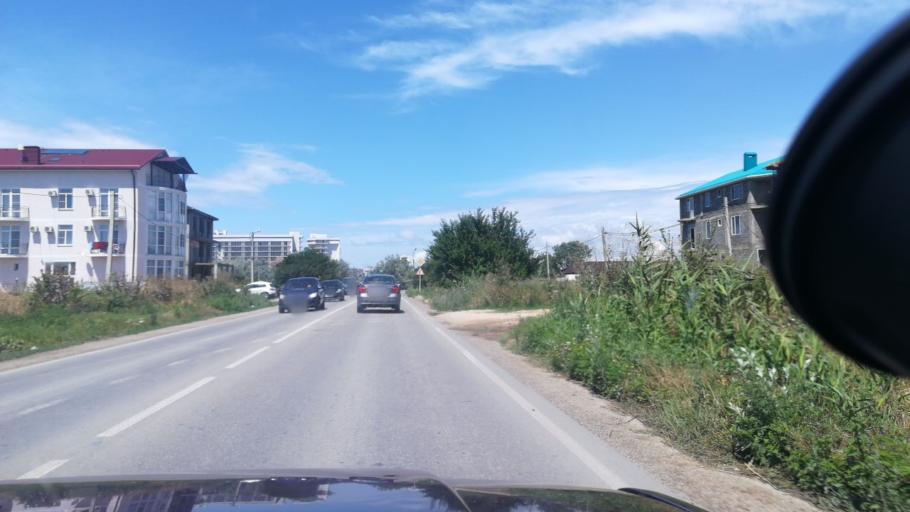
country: RU
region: Krasnodarskiy
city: Vityazevo
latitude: 44.9630
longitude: 37.2920
